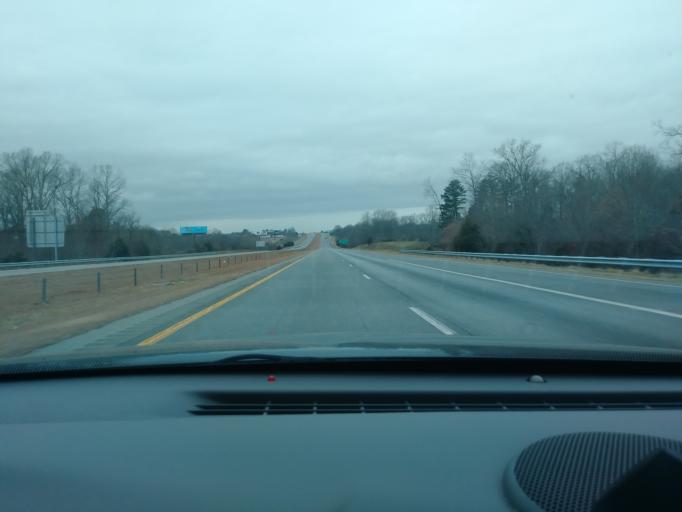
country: US
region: North Carolina
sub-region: Yadkin County
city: Yadkinville
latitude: 36.1169
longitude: -80.7767
